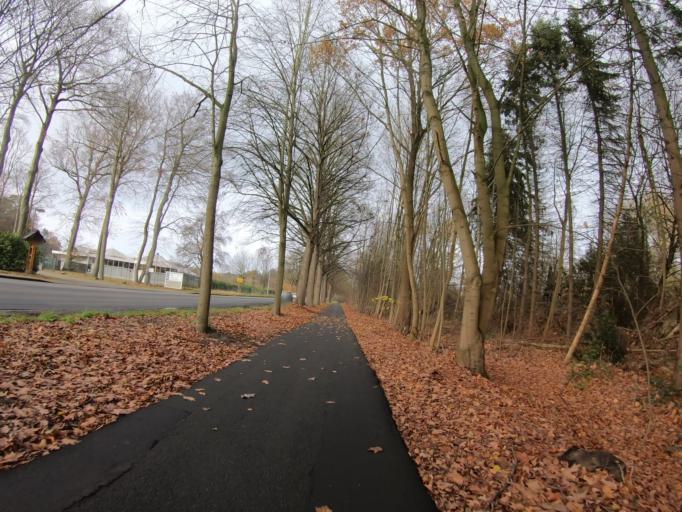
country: DE
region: Lower Saxony
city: Wagenhoff
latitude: 52.5367
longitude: 10.5214
